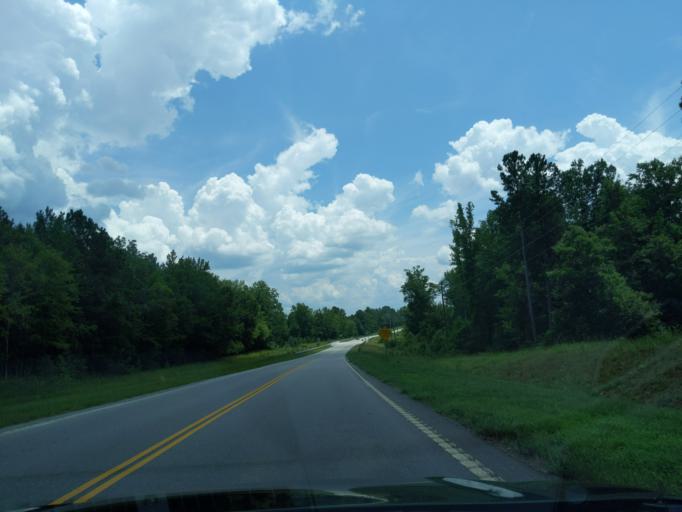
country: US
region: South Carolina
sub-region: Edgefield County
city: Edgefield
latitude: 33.8653
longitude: -81.9885
